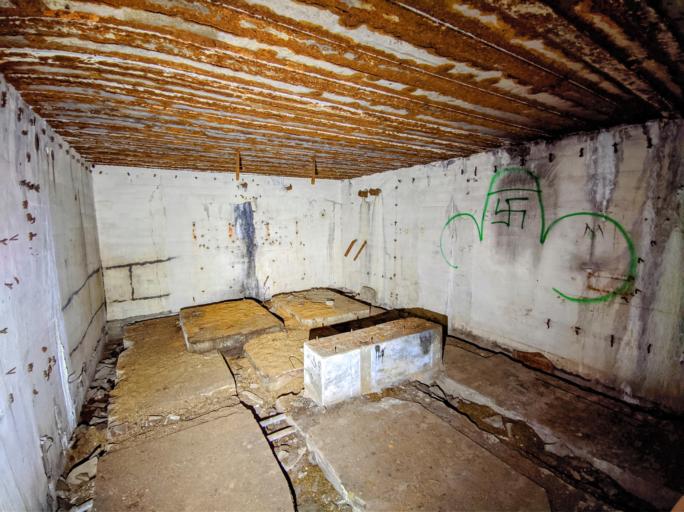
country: PL
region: Lubusz
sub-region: Powiat swiebodzinski
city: Skape
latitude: 52.1655
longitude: 15.4322
